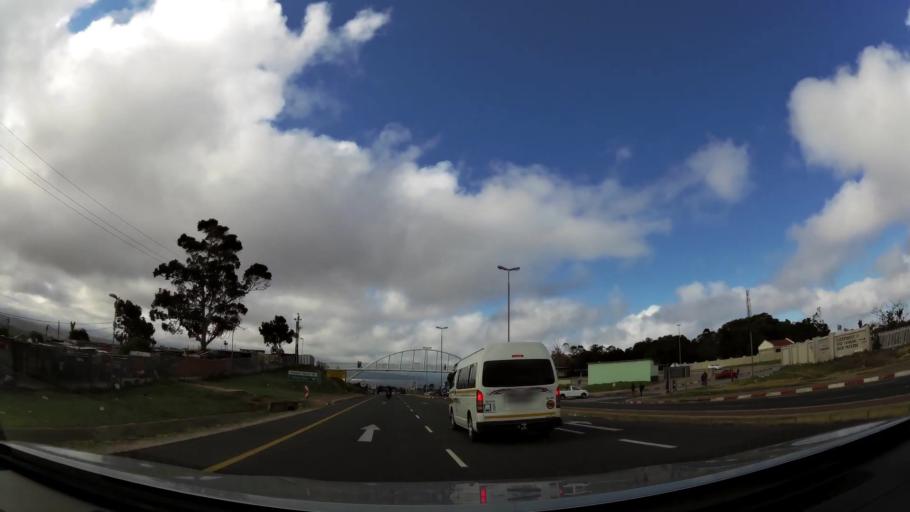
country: ZA
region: Western Cape
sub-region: Eden District Municipality
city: Plettenberg Bay
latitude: -34.0514
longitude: 23.3530
